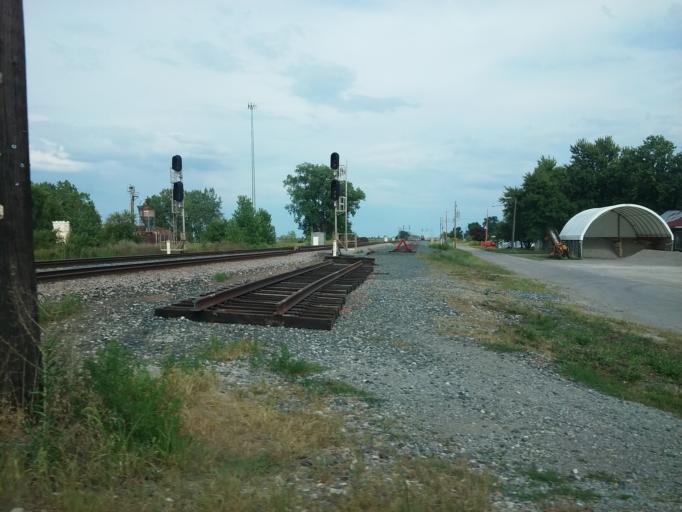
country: US
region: Ohio
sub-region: Hancock County
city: McComb
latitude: 41.1921
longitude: -83.7844
